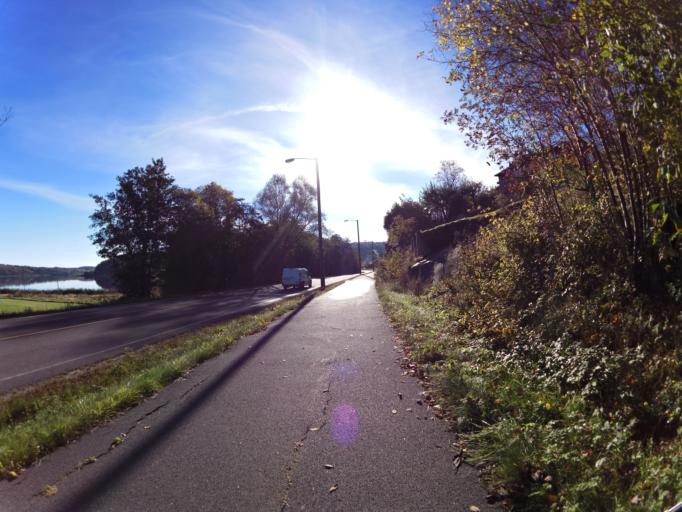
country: NO
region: Ostfold
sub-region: Fredrikstad
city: Fredrikstad
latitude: 59.3032
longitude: 10.9766
